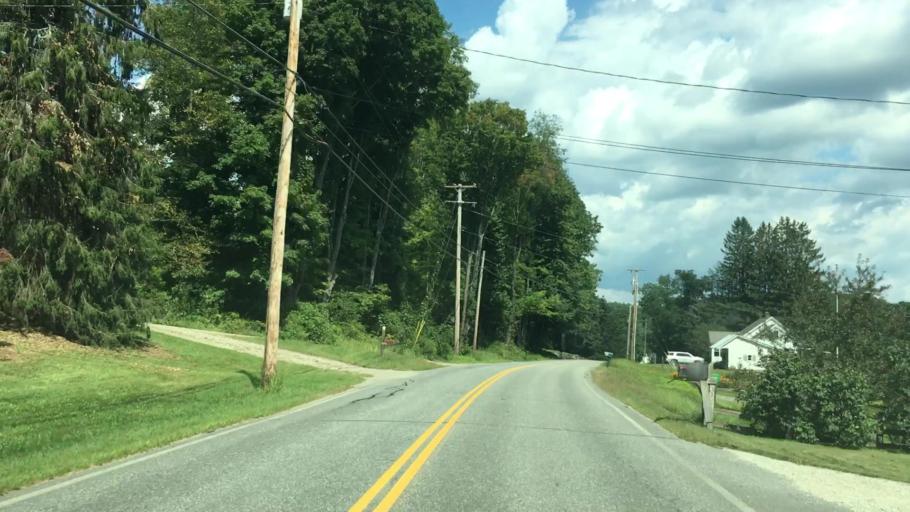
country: US
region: Vermont
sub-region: Windham County
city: West Brattleboro
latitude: 42.8109
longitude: -72.5854
